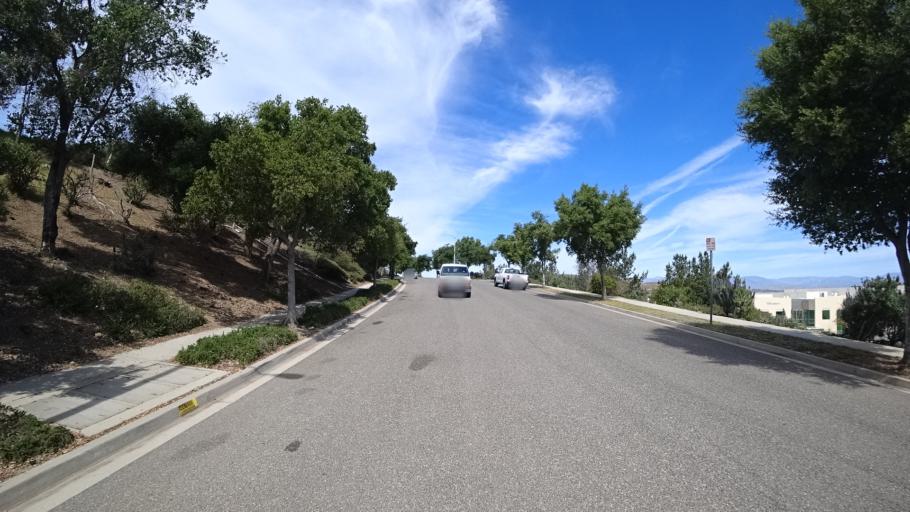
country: US
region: California
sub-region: Ventura County
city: Casa Conejo
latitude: 34.1987
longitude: -118.9297
